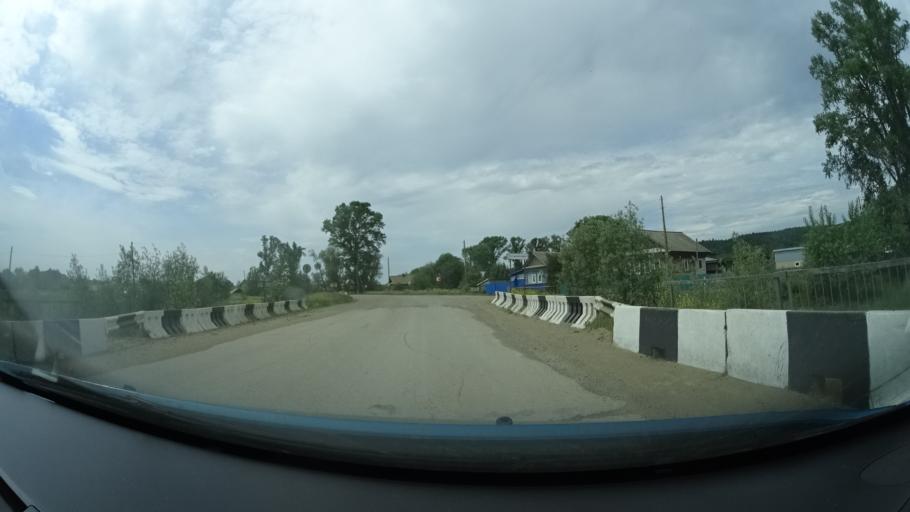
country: RU
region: Perm
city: Barda
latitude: 56.8116
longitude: 55.6705
